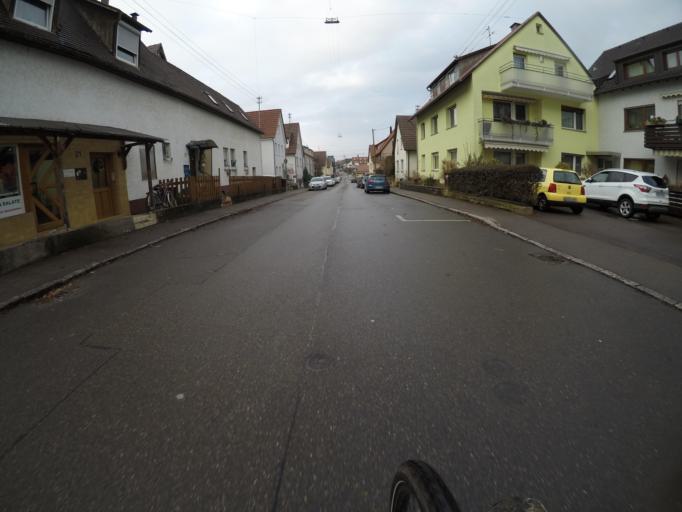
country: DE
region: Baden-Wuerttemberg
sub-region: Regierungsbezirk Stuttgart
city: Filderstadt
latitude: 48.6789
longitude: 9.2214
